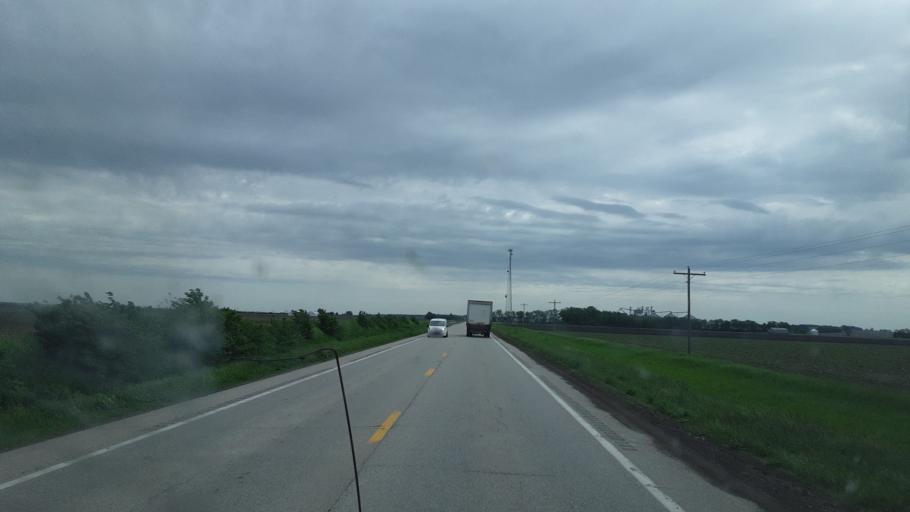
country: US
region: Illinois
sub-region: Mason County
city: Mason City
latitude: 40.3049
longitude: -89.6717
